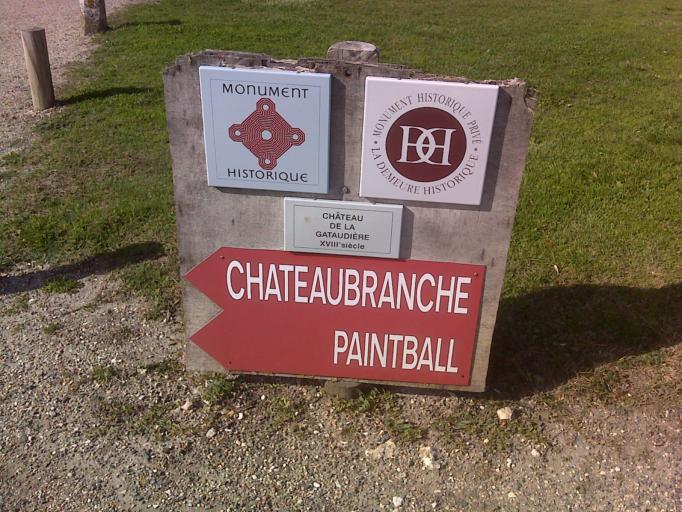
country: FR
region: Poitou-Charentes
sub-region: Departement de la Charente-Maritime
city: Marennes
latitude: 45.8344
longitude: -1.1130
